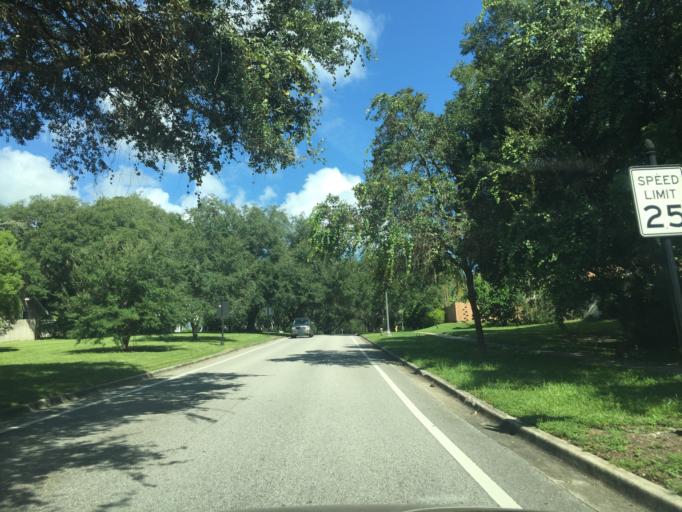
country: US
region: Florida
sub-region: Seminole County
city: Oviedo
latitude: 28.6670
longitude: -81.2596
